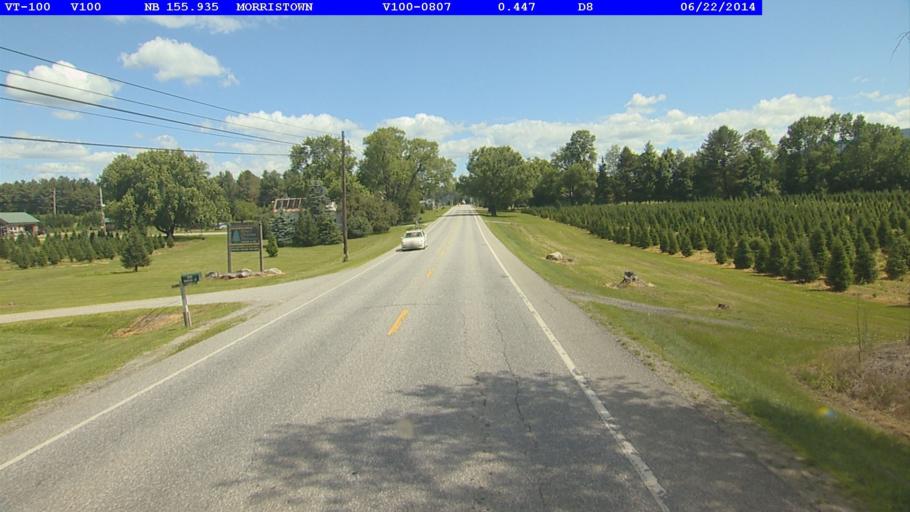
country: US
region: Vermont
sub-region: Lamoille County
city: Morristown
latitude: 44.5005
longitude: -72.6309
